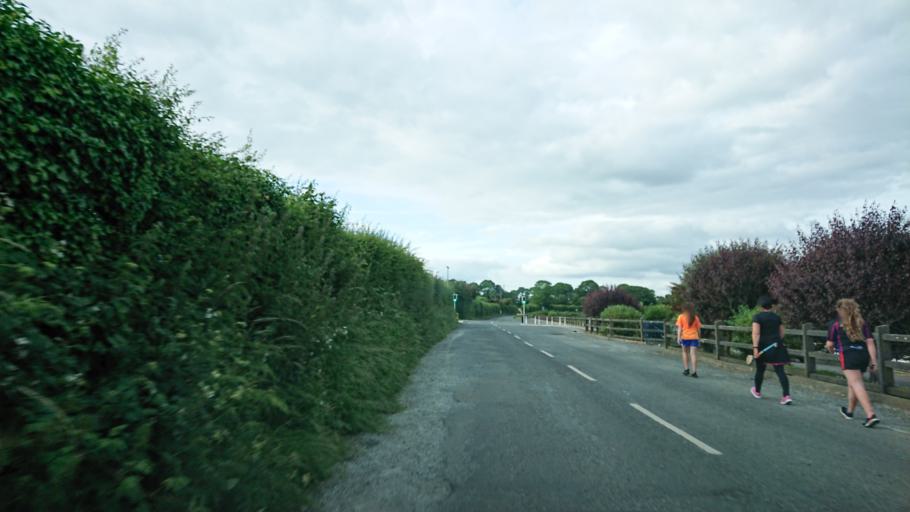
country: IE
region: Munster
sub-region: Waterford
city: Tra Mhor
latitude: 52.2228
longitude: -7.1810
